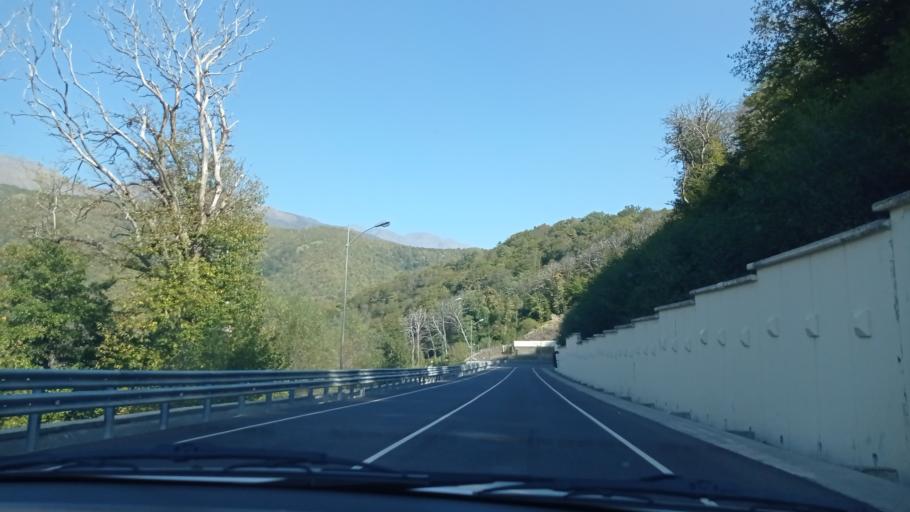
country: RU
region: Krasnodarskiy
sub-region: Sochi City
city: Krasnaya Polyana
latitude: 43.6805
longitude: 40.2431
